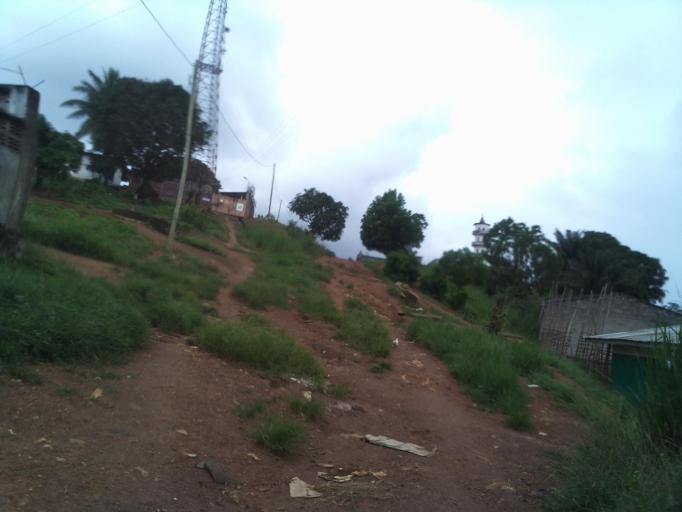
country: SL
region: Eastern Province
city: Kenema
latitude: 7.8597
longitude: -11.1862
